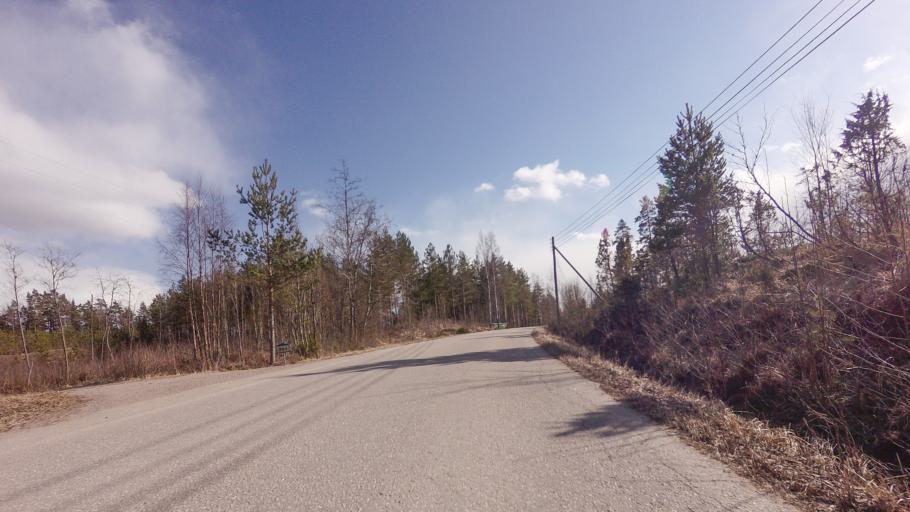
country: FI
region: Varsinais-Suomi
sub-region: Salo
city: Suomusjaervi
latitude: 60.3232
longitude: 23.6521
